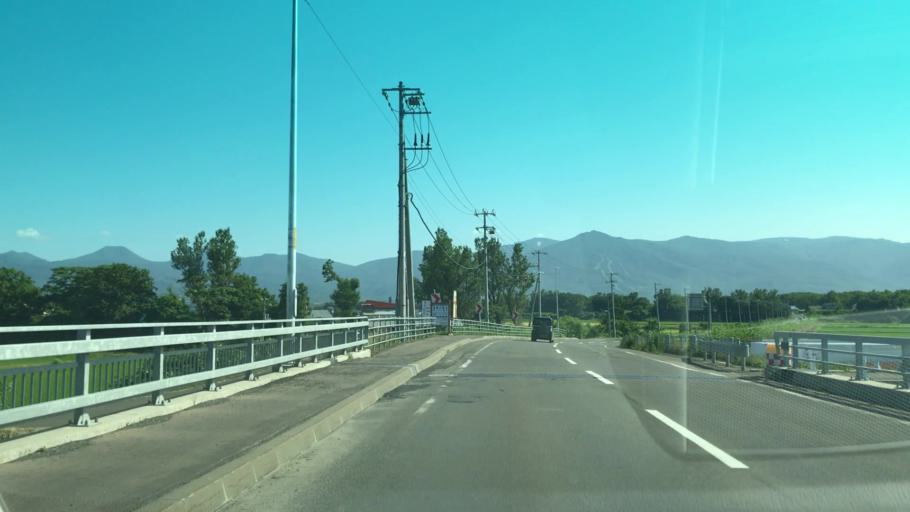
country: JP
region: Hokkaido
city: Iwanai
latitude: 43.0214
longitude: 140.5479
